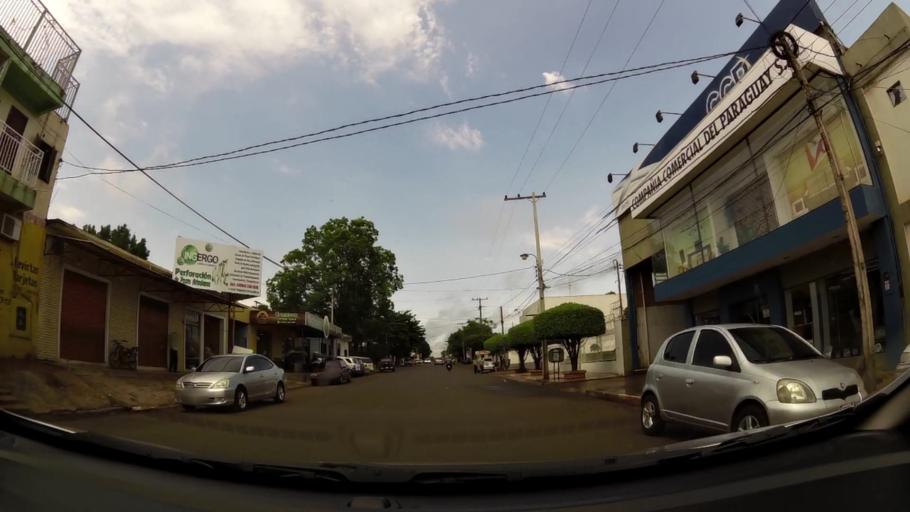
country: PY
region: Alto Parana
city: Ciudad del Este
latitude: -25.5019
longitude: -54.6581
